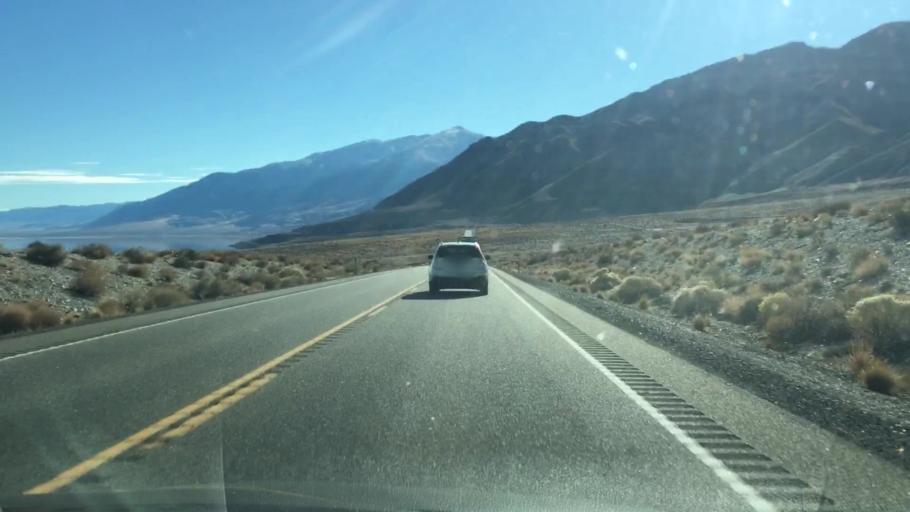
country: US
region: Nevada
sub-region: Mineral County
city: Hawthorne
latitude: 38.7457
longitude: -118.7671
